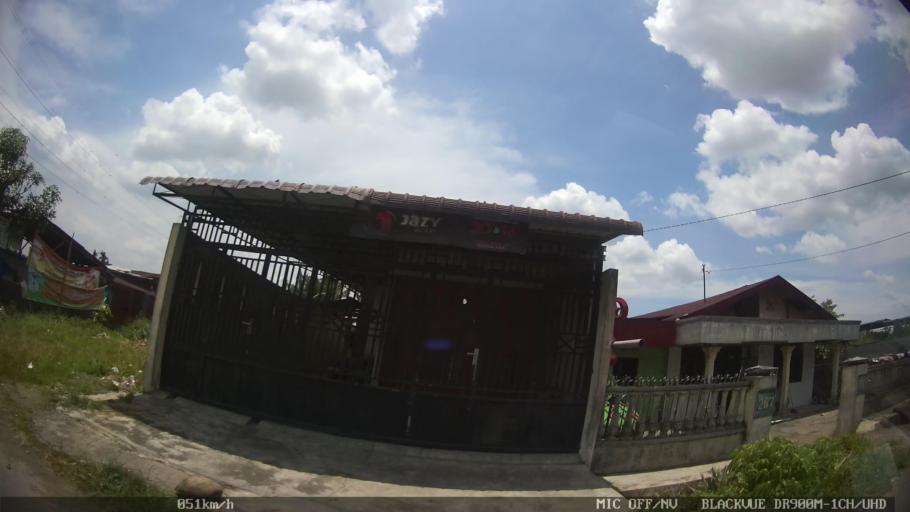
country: ID
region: North Sumatra
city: Binjai
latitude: 3.6278
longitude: 98.5170
